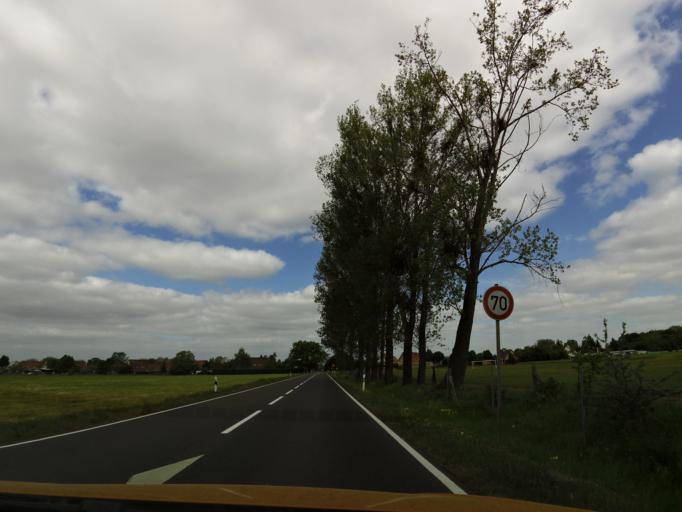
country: DE
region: Saxony-Anhalt
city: Mockern
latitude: 52.1867
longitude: 11.9133
